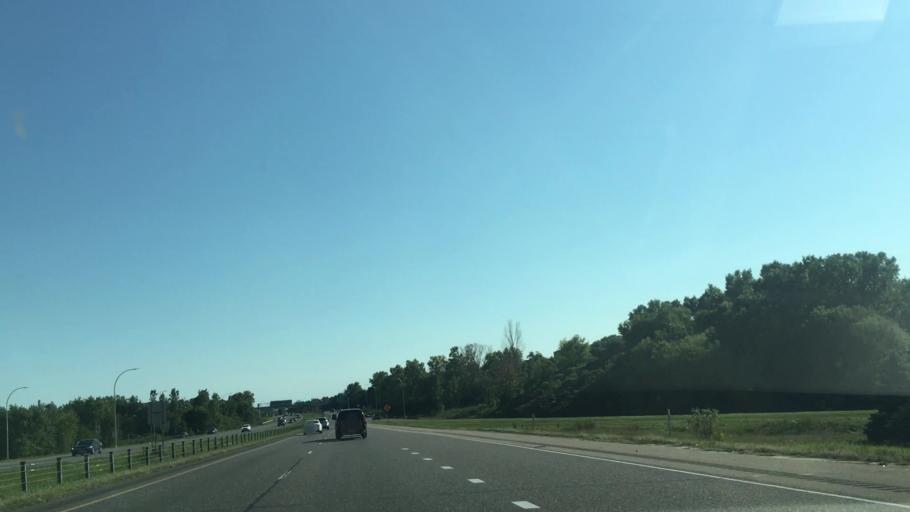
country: US
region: Minnesota
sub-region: Dakota County
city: Inver Grove Heights
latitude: 44.8730
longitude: -93.0610
